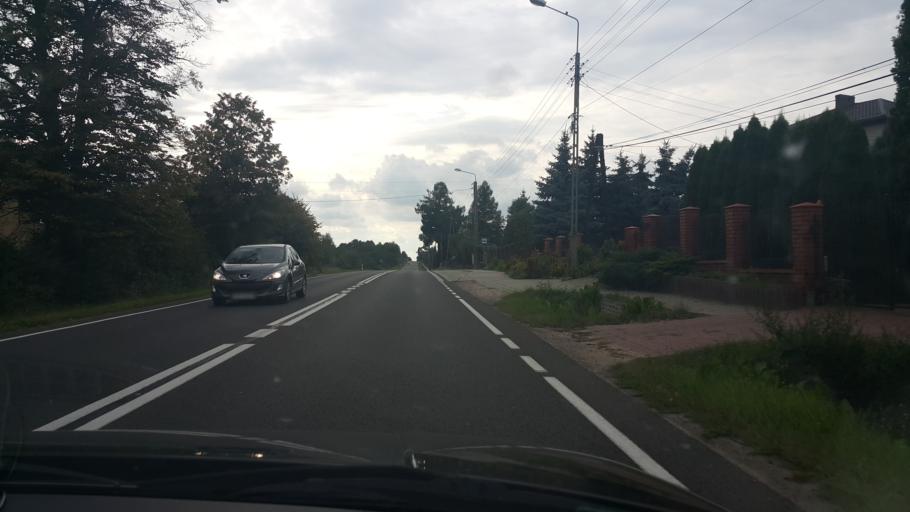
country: PL
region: Swietokrzyskie
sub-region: Powiat skarzyski
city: Blizyn
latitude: 51.1004
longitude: 20.7913
